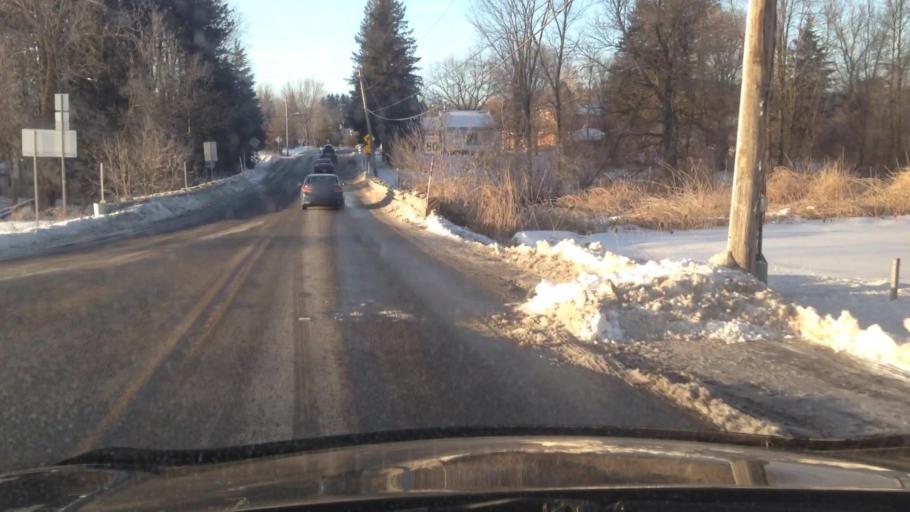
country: CA
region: Quebec
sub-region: Lanaudiere
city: Sainte-Julienne
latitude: 45.9145
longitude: -73.7368
